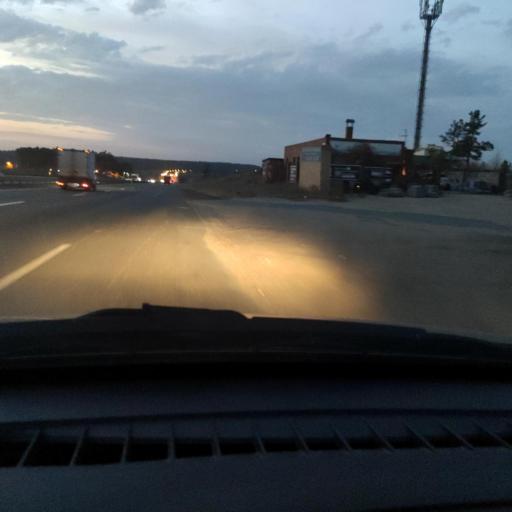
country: RU
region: Samara
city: Zhigulevsk
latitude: 53.5213
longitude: 49.5309
